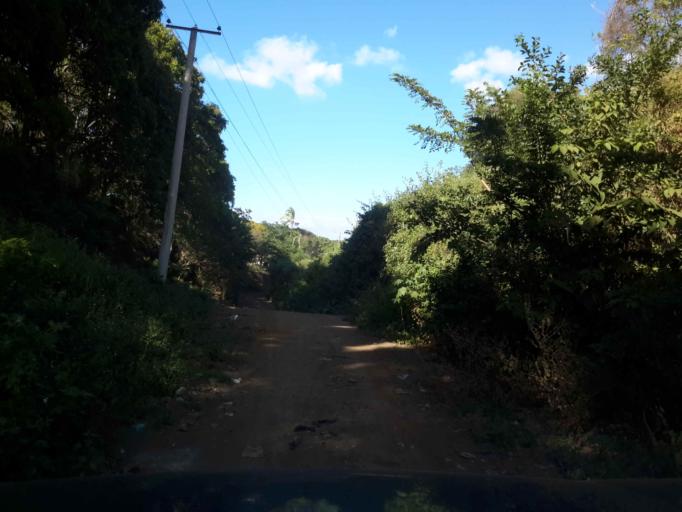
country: NI
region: Managua
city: Managua
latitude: 12.0672
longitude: -86.2538
